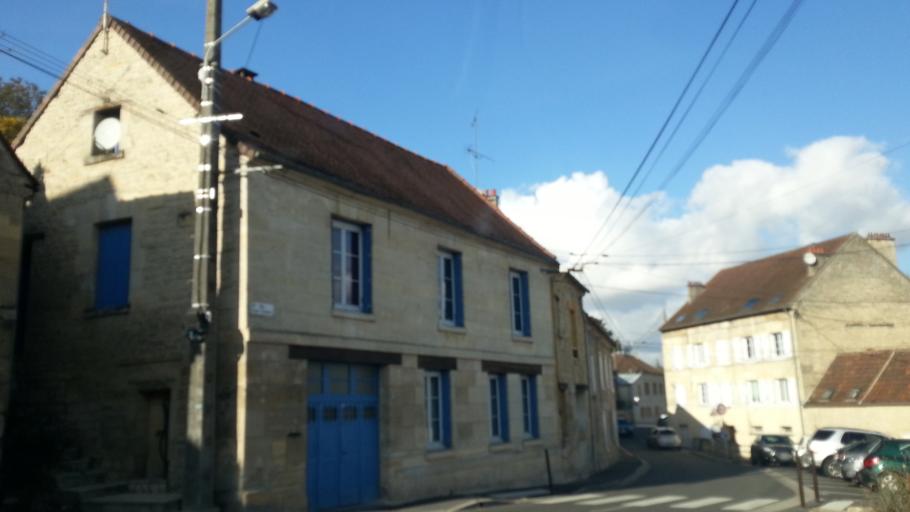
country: FR
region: Picardie
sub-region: Departement de l'Oise
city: Thiverny
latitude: 49.2553
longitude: 2.4008
